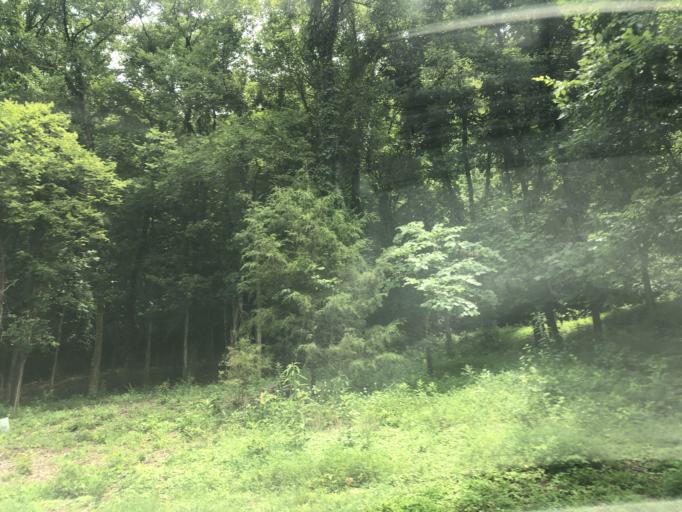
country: US
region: Tennessee
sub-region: Davidson County
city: Forest Hills
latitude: 36.0781
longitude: -86.8269
